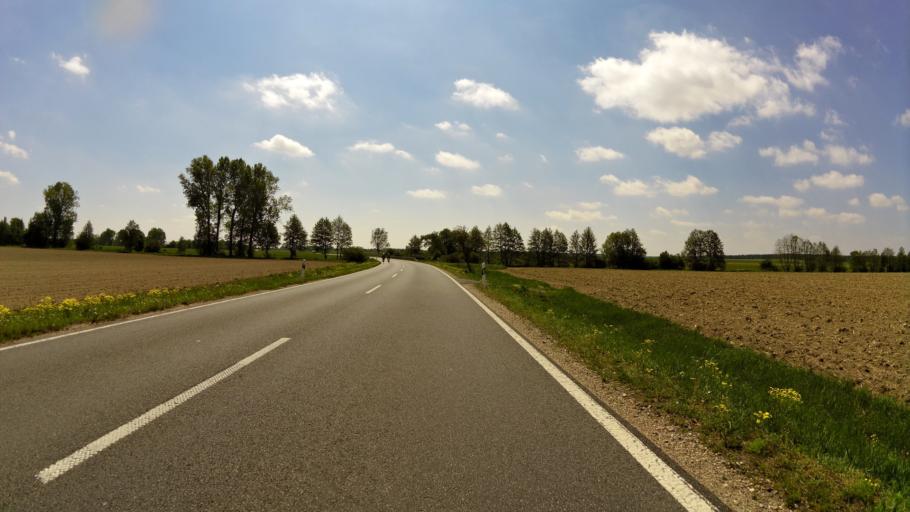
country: DE
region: Saxony
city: Belgern
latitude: 51.4591
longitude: 13.1556
